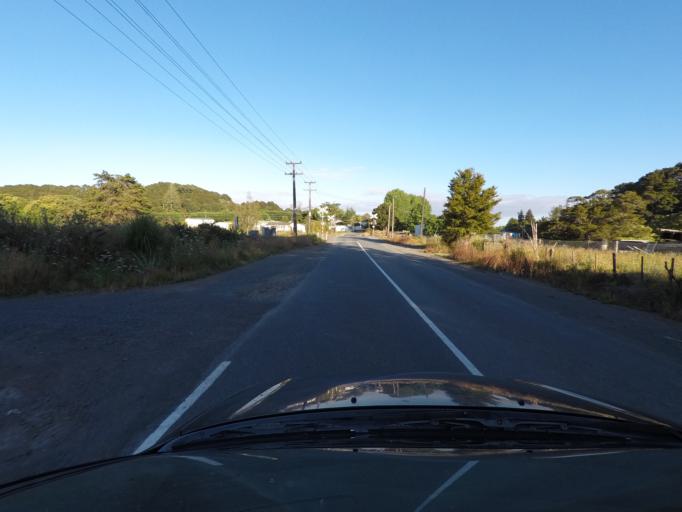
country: NZ
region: Northland
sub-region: Whangarei
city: Whangarei
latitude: -35.6423
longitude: 174.2991
